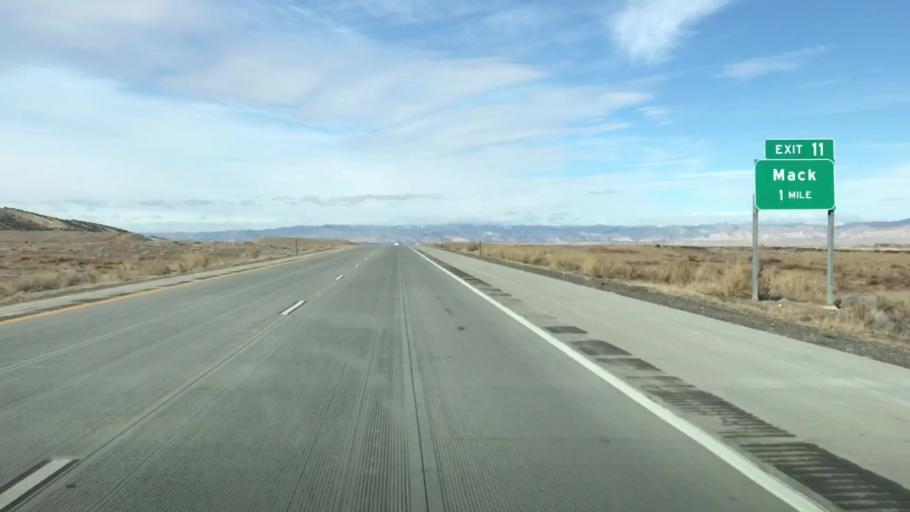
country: US
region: Colorado
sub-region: Mesa County
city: Loma
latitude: 39.2018
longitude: -108.8520
